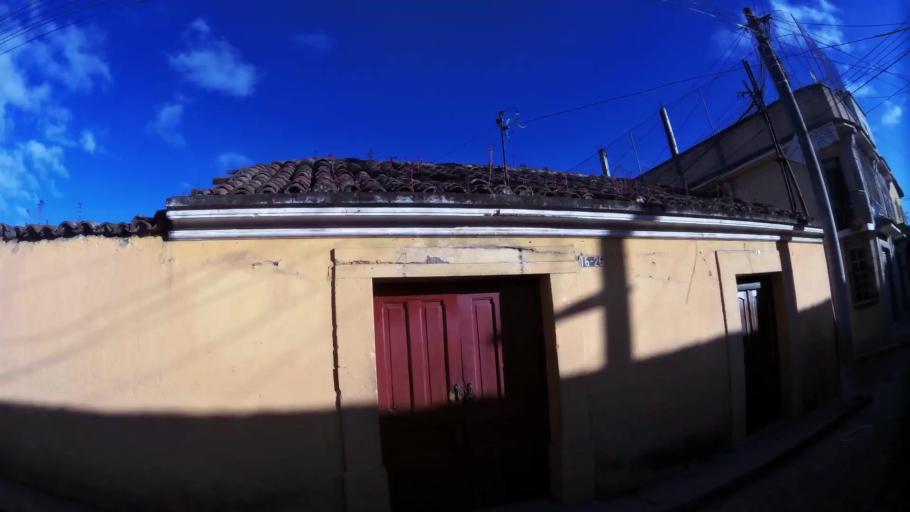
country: GT
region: Quetzaltenango
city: Quetzaltenango
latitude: 14.8327
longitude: -91.5234
